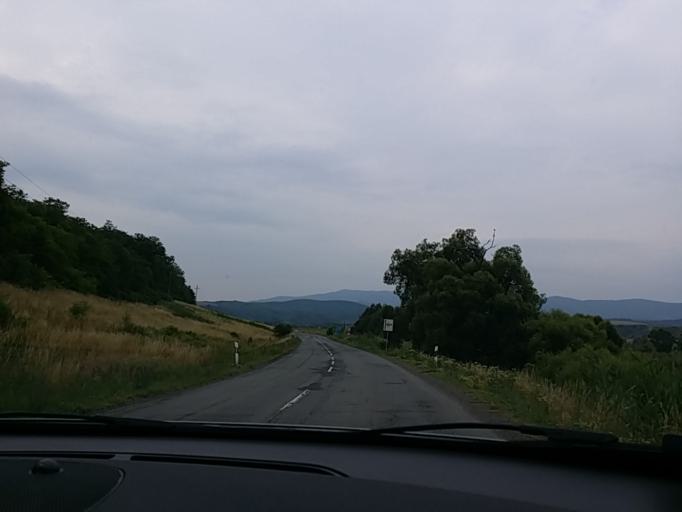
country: HU
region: Nograd
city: Batonyterenye
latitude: 48.0017
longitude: 19.8492
